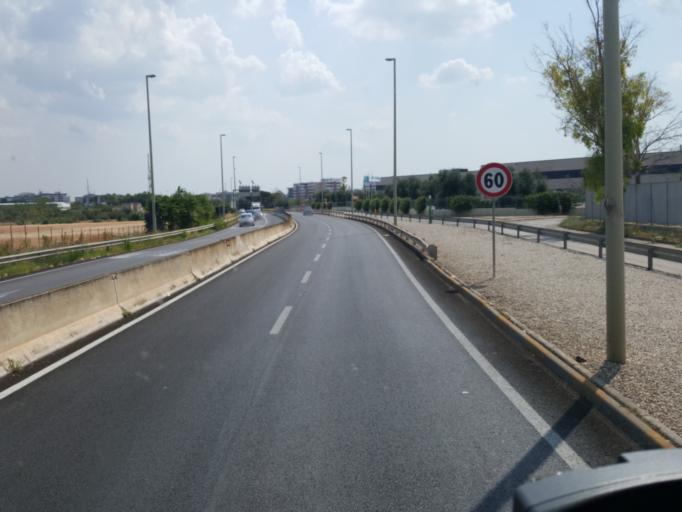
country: IT
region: Apulia
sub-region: Provincia di Bari
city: Modugno
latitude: 41.0972
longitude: 16.7731
